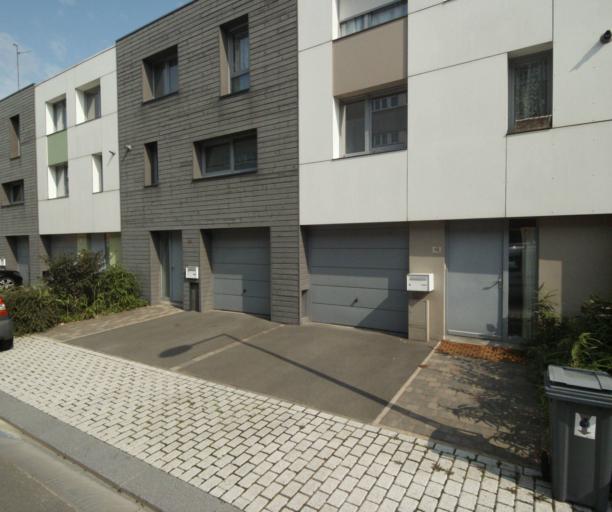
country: FR
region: Nord-Pas-de-Calais
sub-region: Departement du Nord
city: Lambersart
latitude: 50.6547
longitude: 3.0314
